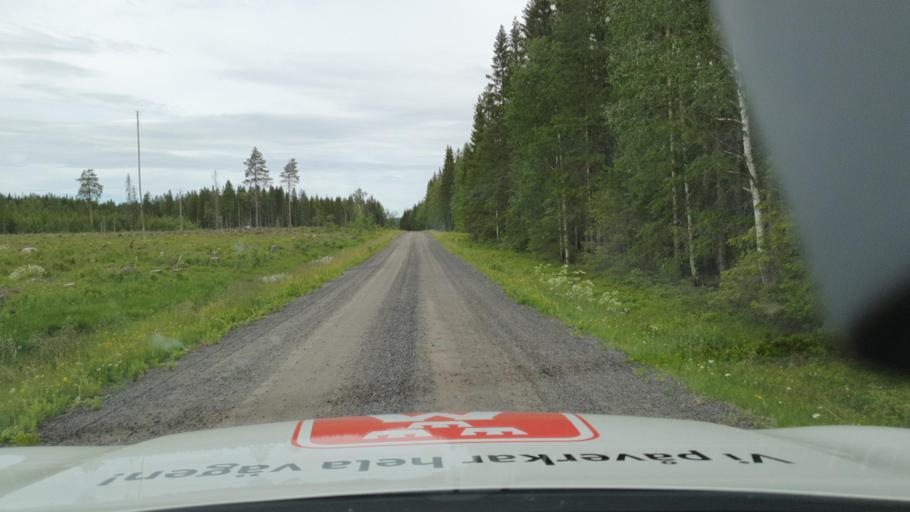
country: SE
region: Vaesterbotten
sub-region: Skelleftea Kommun
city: Burtraesk
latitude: 64.3808
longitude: 20.6147
